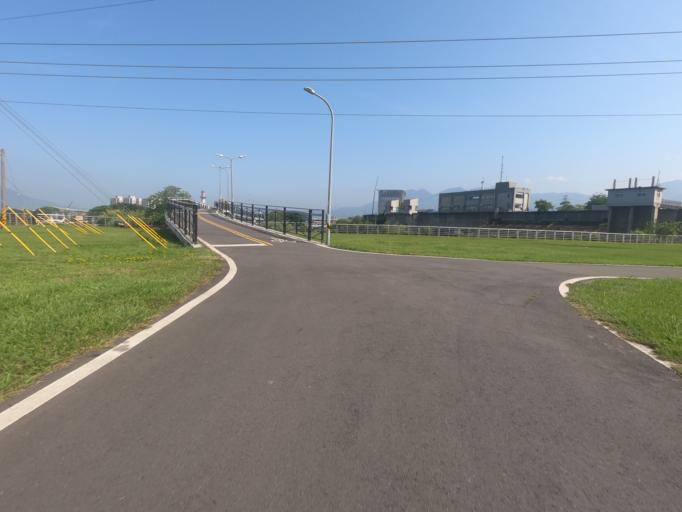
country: TW
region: Taipei
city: Taipei
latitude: 25.0947
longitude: 121.5111
